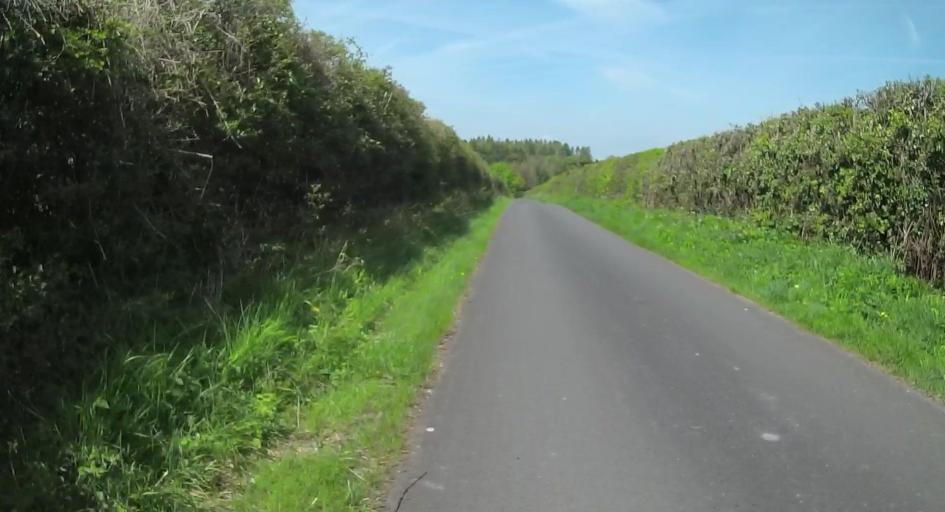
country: GB
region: England
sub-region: Hampshire
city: Romsey
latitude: 51.0869
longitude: -1.4924
